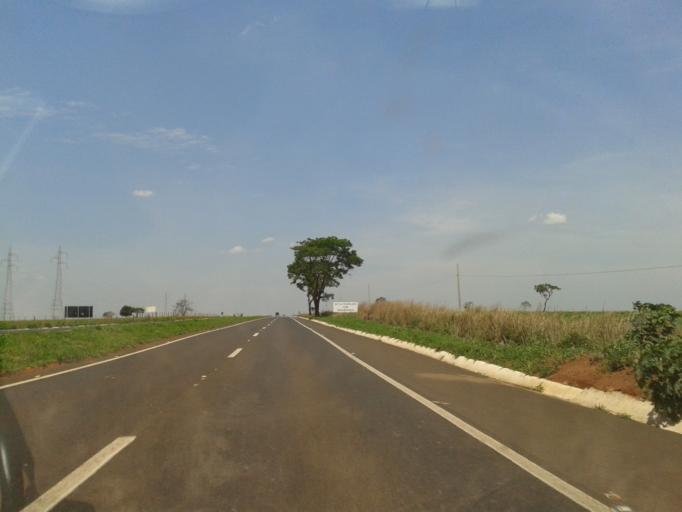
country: BR
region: Minas Gerais
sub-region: Monte Alegre De Minas
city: Monte Alegre de Minas
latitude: -18.8502
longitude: -48.8341
